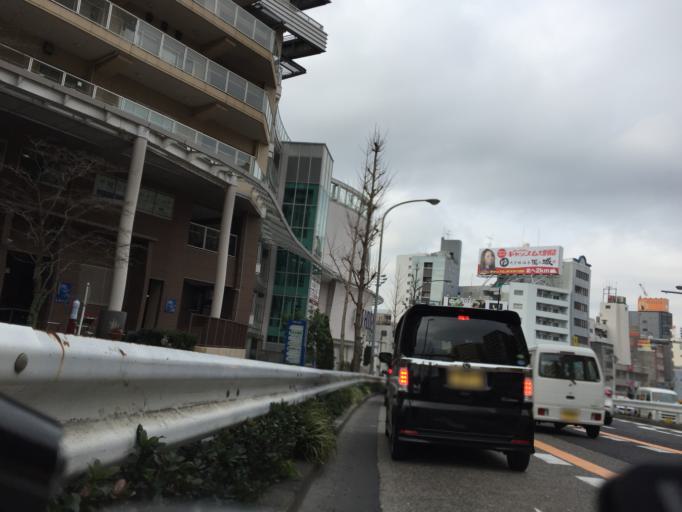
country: JP
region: Aichi
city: Nagoya-shi
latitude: 35.1695
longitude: 136.9288
